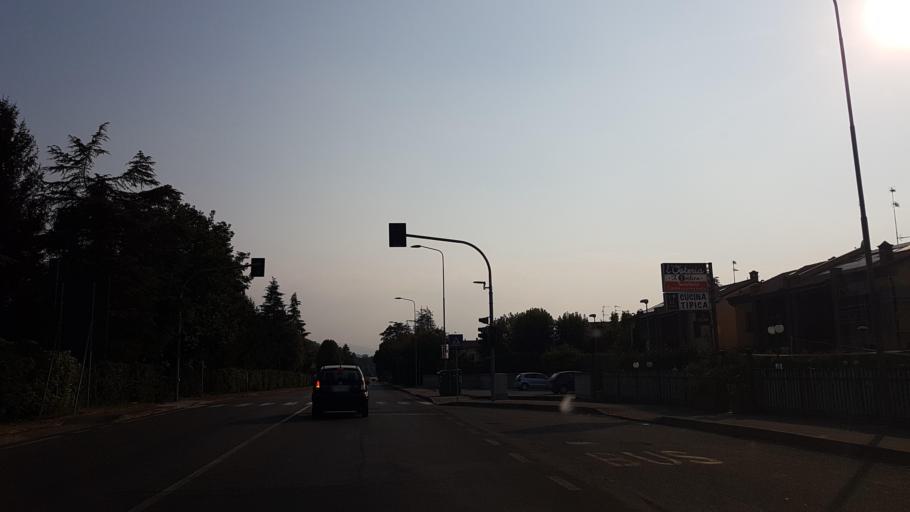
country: IT
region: Emilia-Romagna
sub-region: Provincia di Parma
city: Gaiano
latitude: 44.7394
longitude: 10.1913
